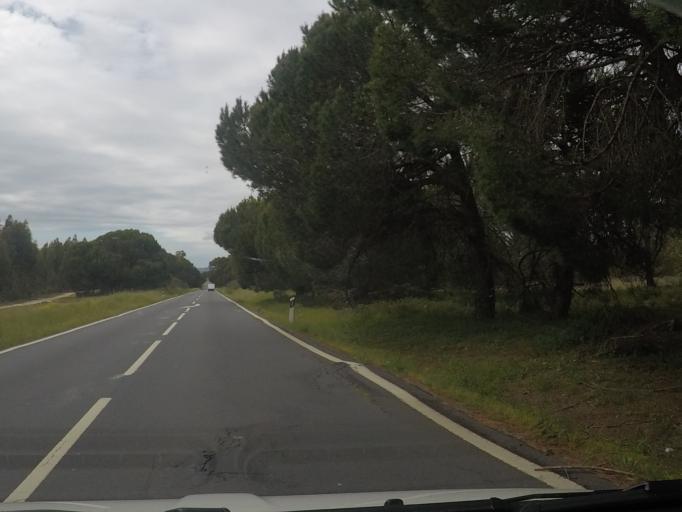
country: PT
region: Setubal
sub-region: Sines
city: Porto Covo
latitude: 37.8804
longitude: -8.7460
